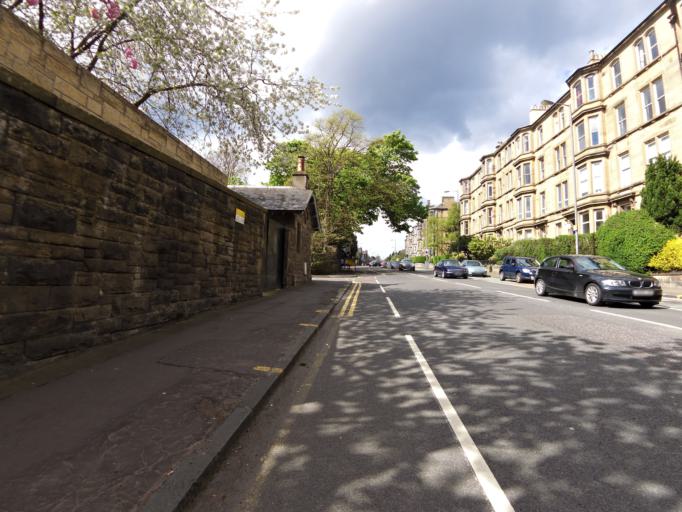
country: GB
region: Scotland
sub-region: Edinburgh
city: Edinburgh
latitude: 55.9344
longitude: -3.1678
